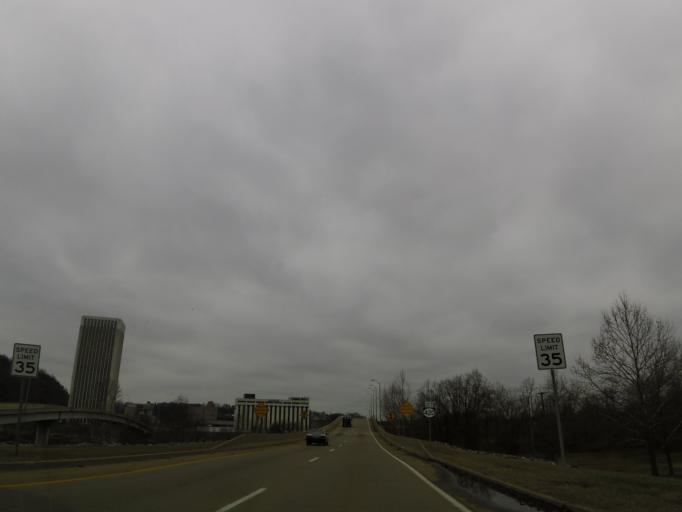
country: US
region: Kentucky
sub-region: Franklin County
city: Frankfort
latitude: 38.2048
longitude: -84.8827
